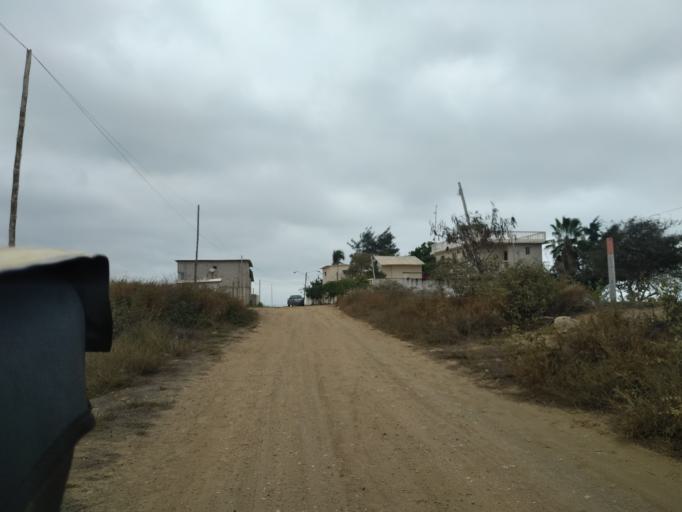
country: EC
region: Santa Elena
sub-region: Canton Santa Elena
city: Santa Elena
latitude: -2.2050
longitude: -80.8667
